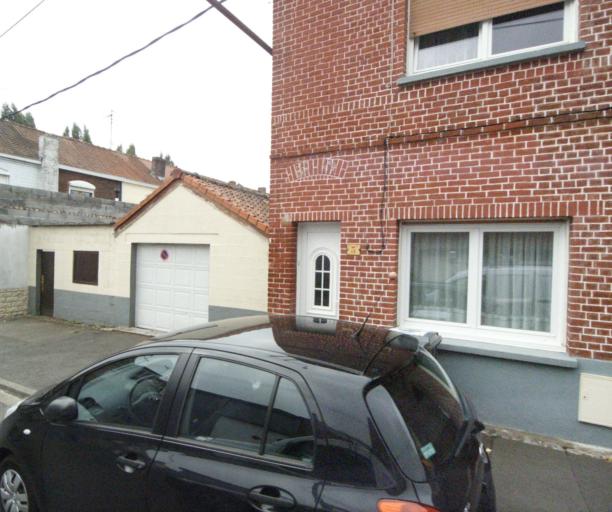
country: FR
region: Nord-Pas-de-Calais
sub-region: Departement du Nord
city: Wasquehal
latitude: 50.6686
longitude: 3.1237
